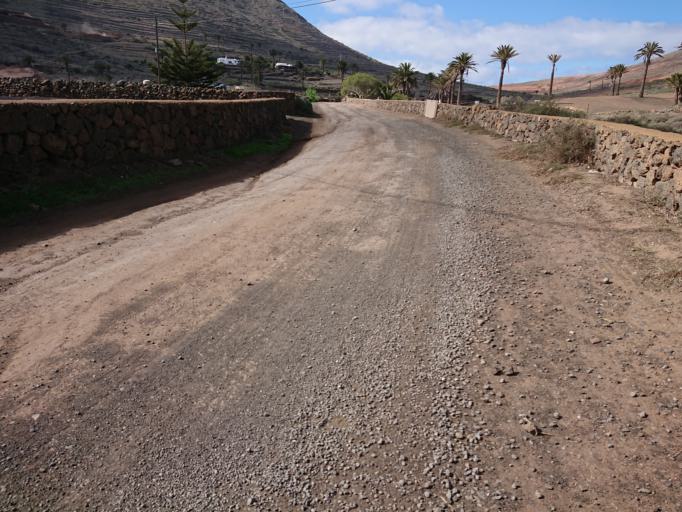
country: ES
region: Canary Islands
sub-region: Provincia de Las Palmas
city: Haria
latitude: 29.1438
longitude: -13.5066
